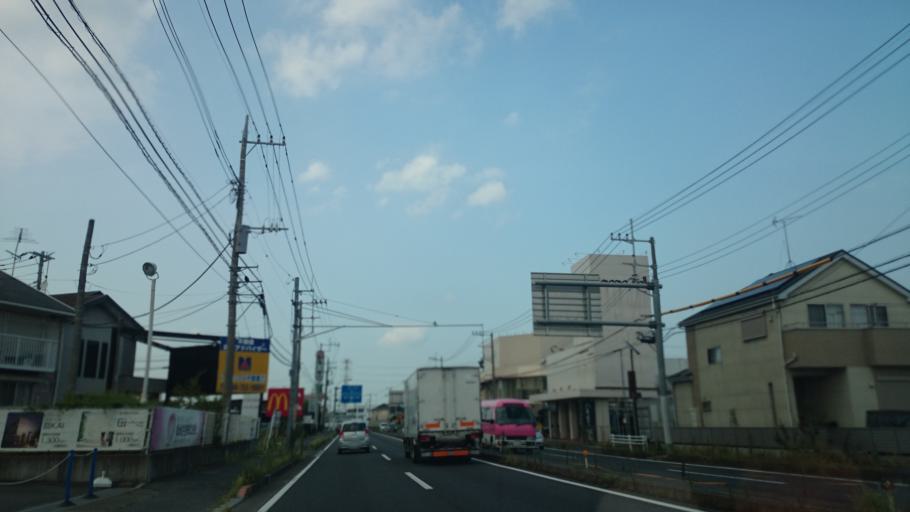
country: JP
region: Saitama
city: Kasukabe
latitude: 35.9685
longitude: 139.7353
